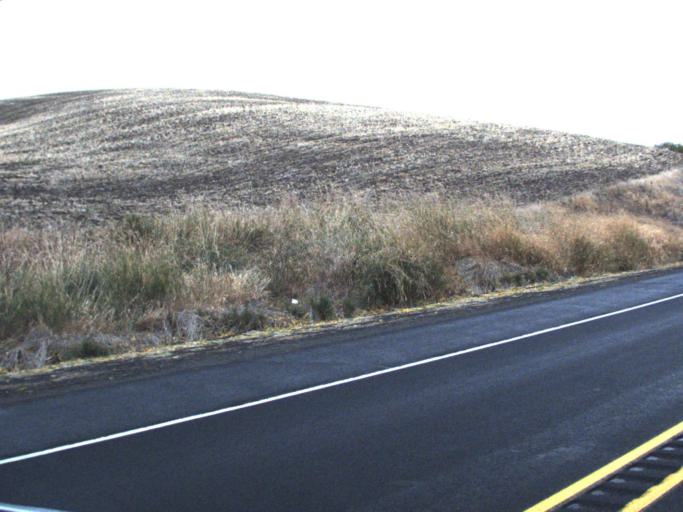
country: US
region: Washington
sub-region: Whitman County
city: Pullman
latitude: 46.7419
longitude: -117.2323
